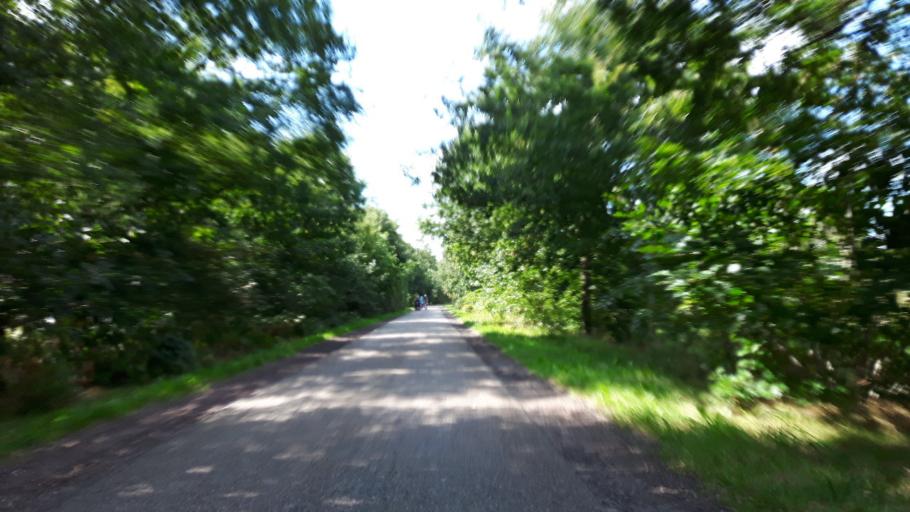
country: NL
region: Groningen
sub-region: Gemeente Leek
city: Leek
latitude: 53.0842
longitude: 6.2970
